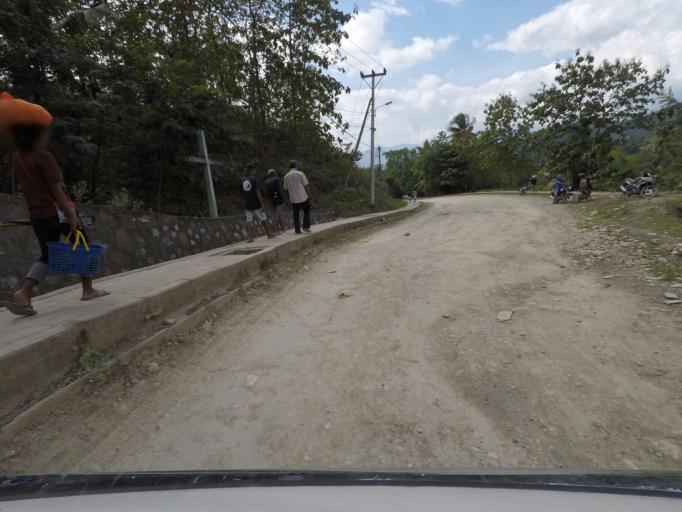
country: TL
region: Viqueque
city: Viqueque
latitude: -8.8643
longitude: 126.3619
